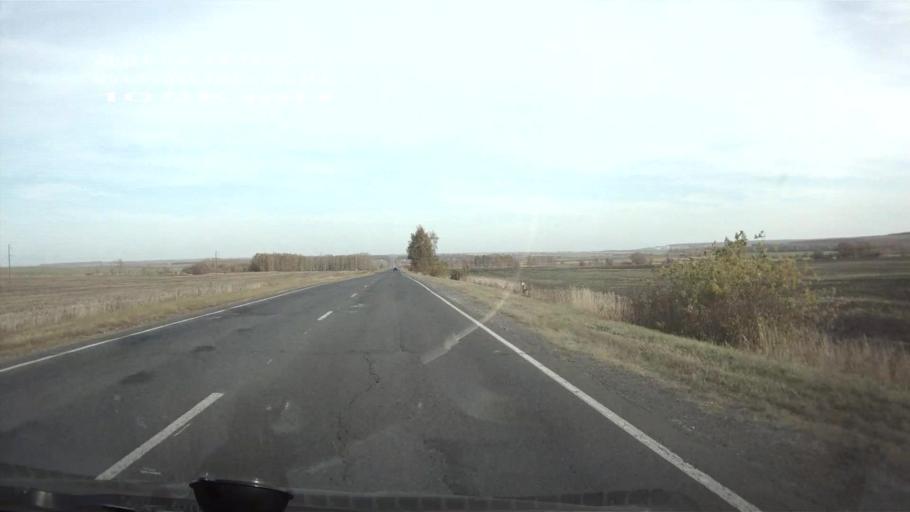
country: RU
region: Mordoviya
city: Atyashevo
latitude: 54.5397
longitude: 45.9332
